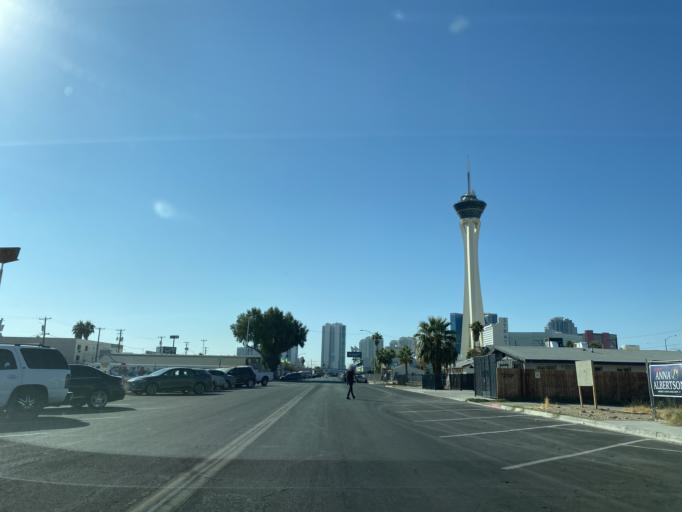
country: US
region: Nevada
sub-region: Clark County
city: Las Vegas
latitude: 36.1542
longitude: -115.1526
